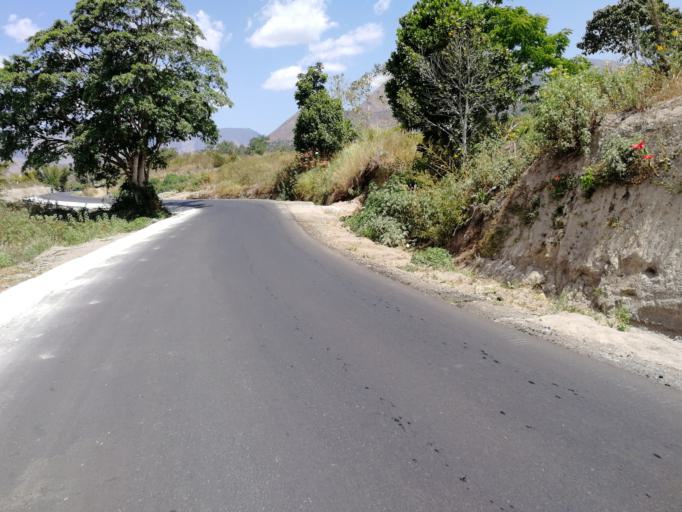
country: ID
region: West Nusa Tenggara
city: Sembalunlawang
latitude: -8.3515
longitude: 116.5098
